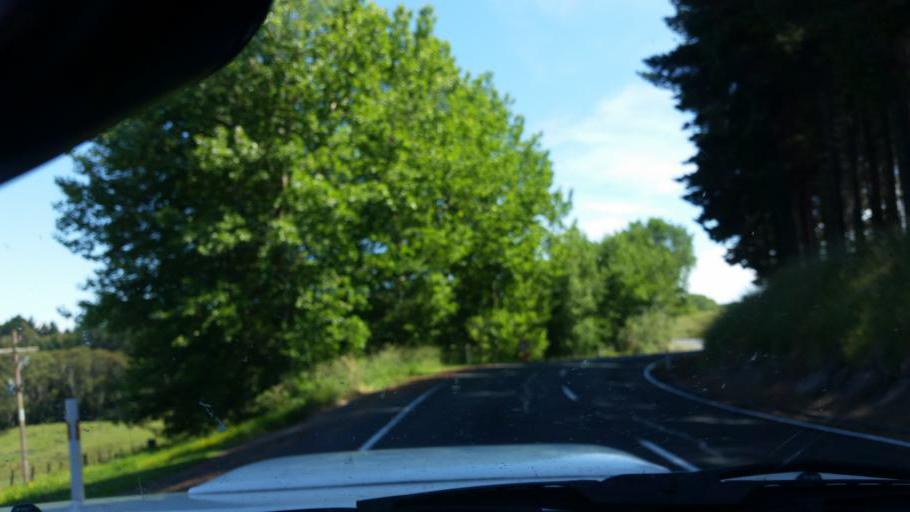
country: NZ
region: Auckland
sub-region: Auckland
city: Wellsford
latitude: -36.2021
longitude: 174.3964
